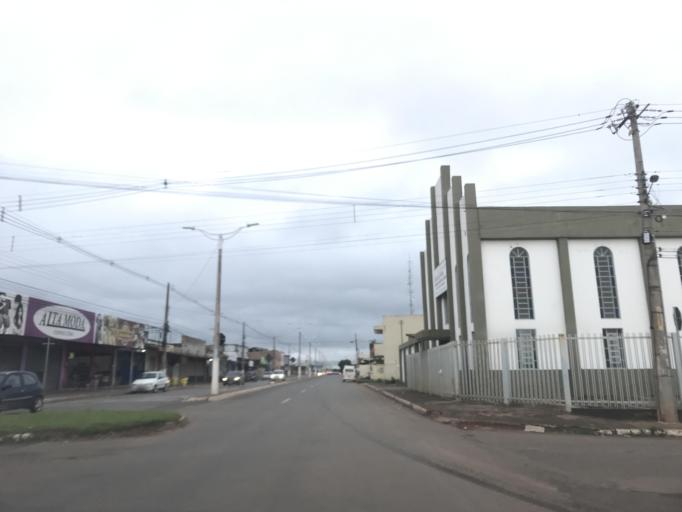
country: BR
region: Goias
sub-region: Luziania
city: Luziania
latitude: -16.2050
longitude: -47.9248
